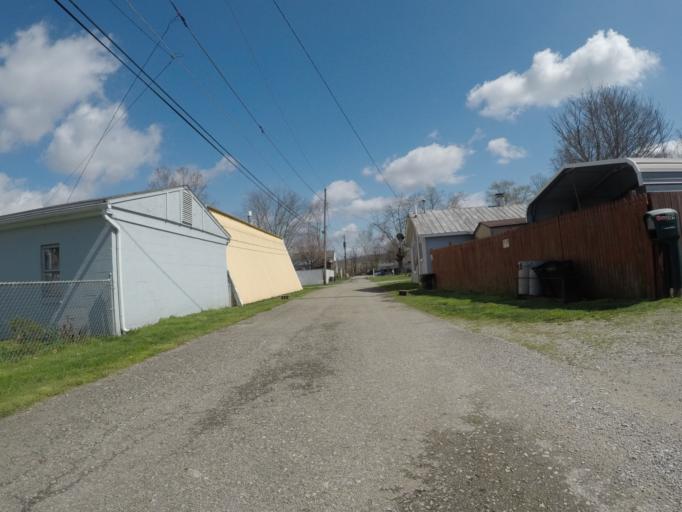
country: US
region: West Virginia
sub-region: Wayne County
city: Ceredo
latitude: 38.3958
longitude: -82.5680
